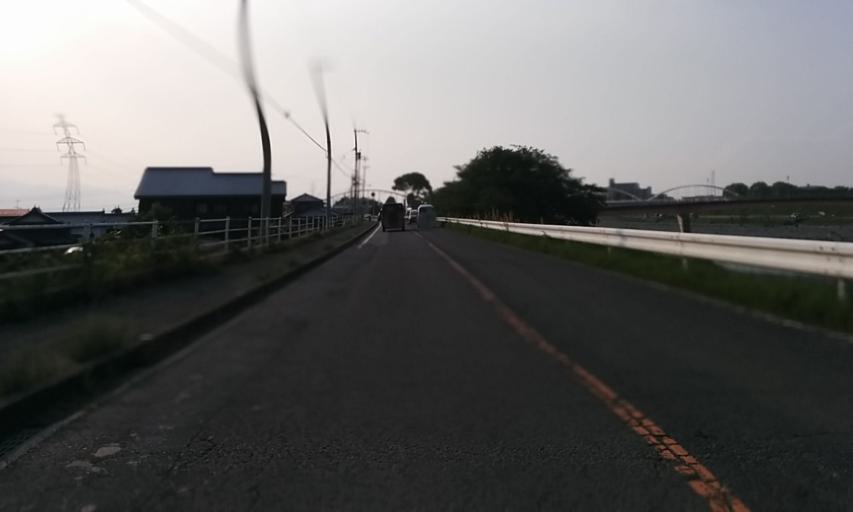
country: JP
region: Ehime
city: Saijo
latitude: 33.8985
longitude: 133.1906
